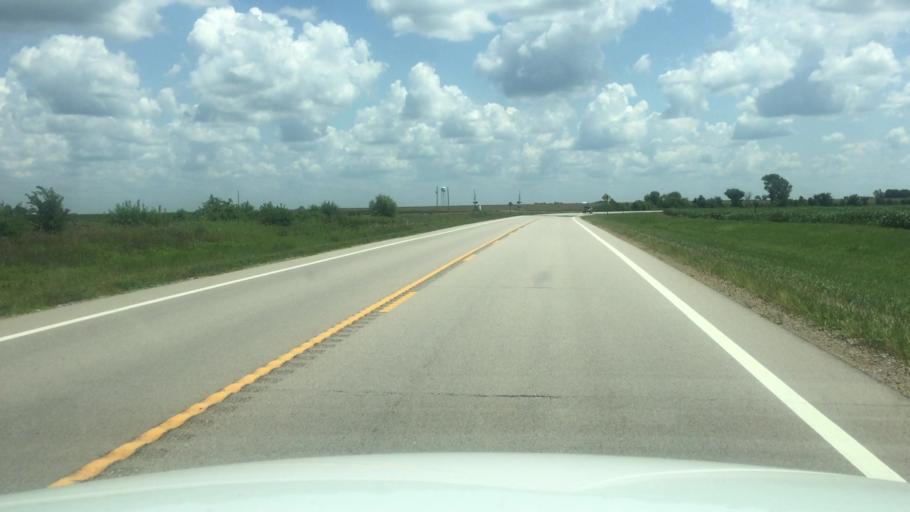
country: US
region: Kansas
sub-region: Brown County
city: Horton
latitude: 39.6521
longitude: -95.3617
